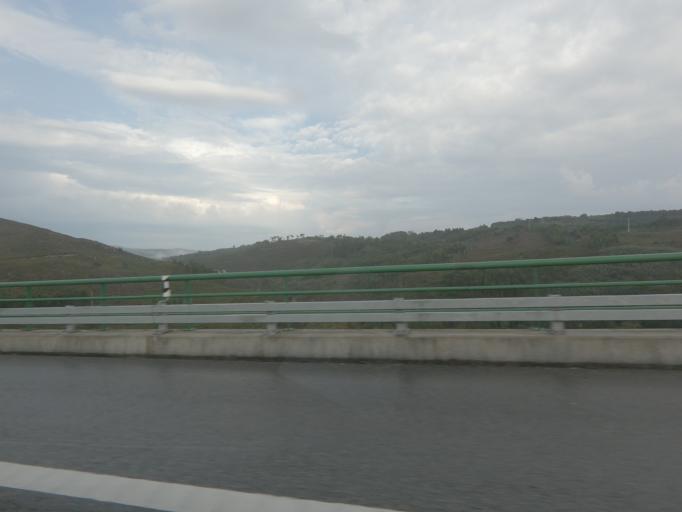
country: PT
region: Viseu
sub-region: Viseu
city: Campo
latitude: 40.7490
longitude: -7.9237
